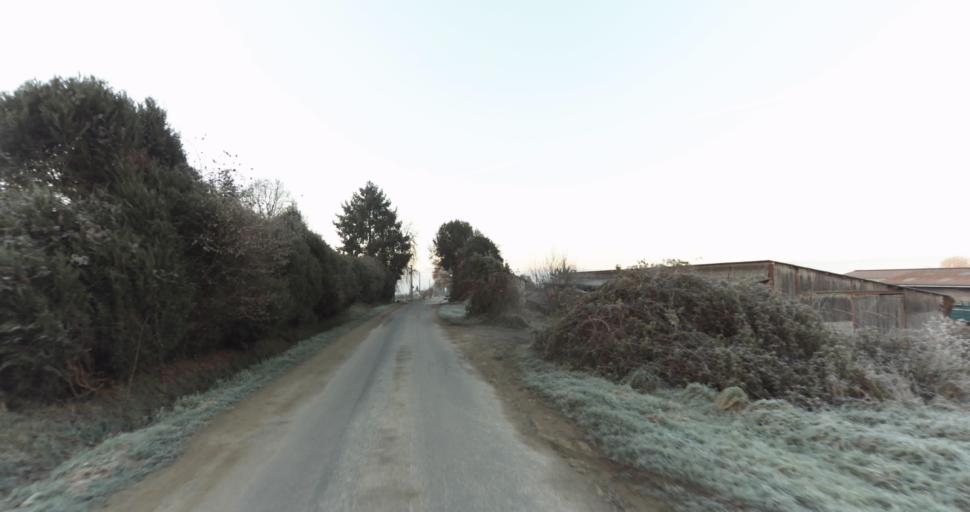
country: FR
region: Limousin
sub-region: Departement de la Haute-Vienne
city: Aixe-sur-Vienne
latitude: 45.8083
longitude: 1.1308
